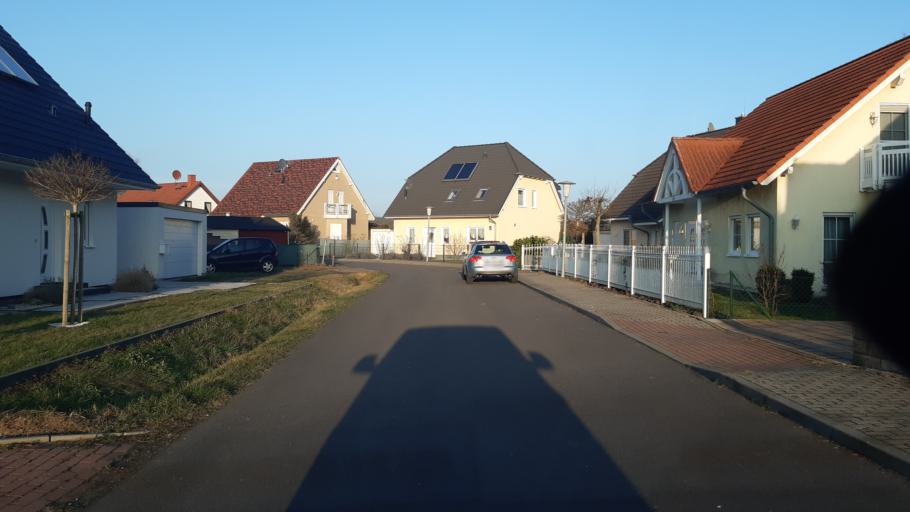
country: DE
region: Brandenburg
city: Velten
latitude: 52.7123
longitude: 13.1518
